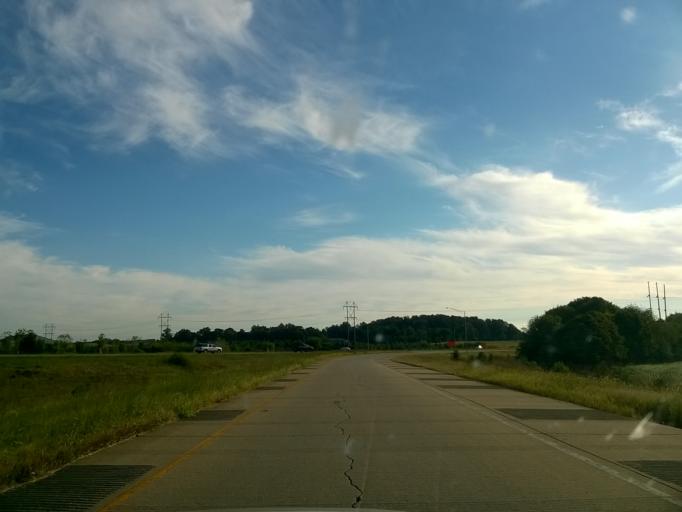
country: US
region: Indiana
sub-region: Gibson County
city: Haubstadt
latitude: 38.1693
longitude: -87.4664
